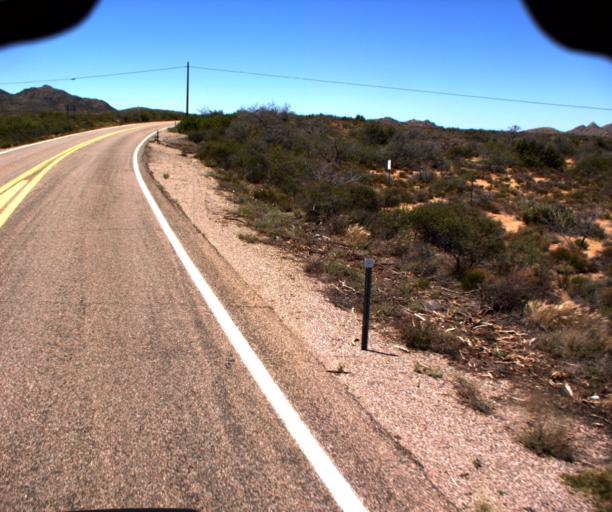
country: US
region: Arizona
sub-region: Yavapai County
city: Congress
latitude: 34.4317
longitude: -112.9186
